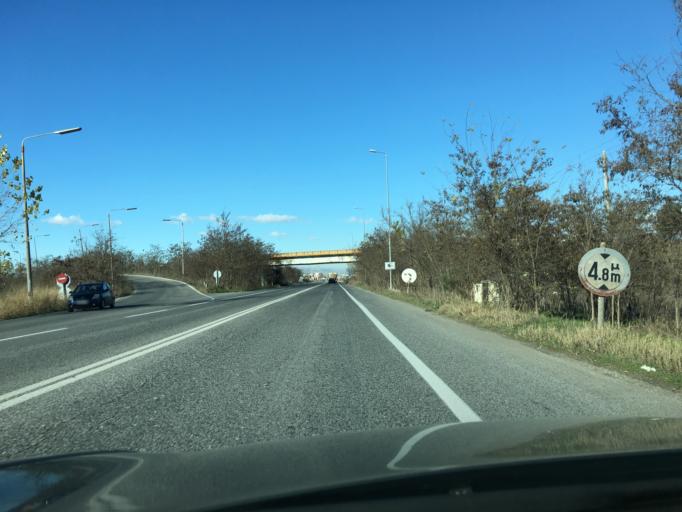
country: GR
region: Thessaly
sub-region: Nomos Larisis
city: Nikaia
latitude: 39.6004
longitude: 22.4455
